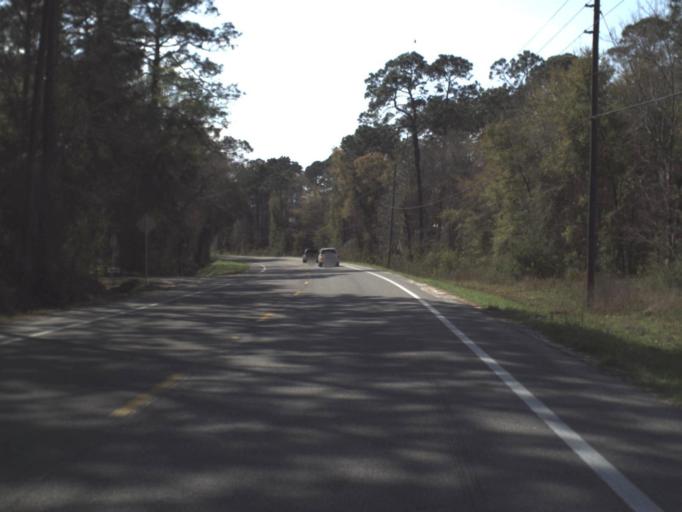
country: US
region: Florida
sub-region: Wakulla County
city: Crawfordville
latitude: 30.0770
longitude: -84.4174
